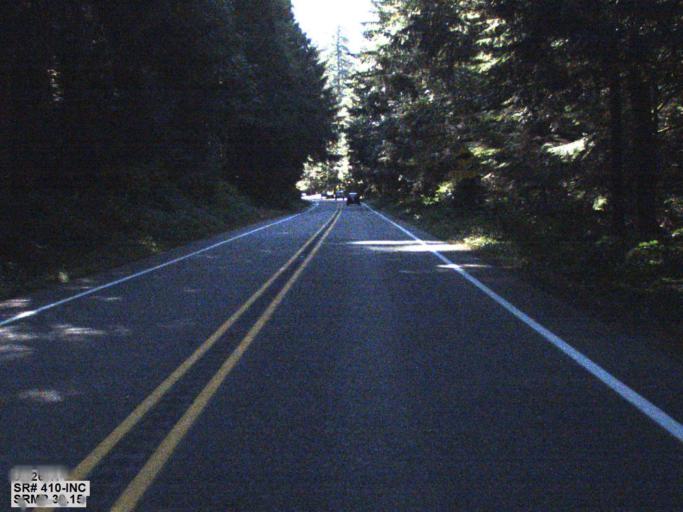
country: US
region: Washington
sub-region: King County
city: Enumclaw
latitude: 47.1590
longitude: -121.7294
